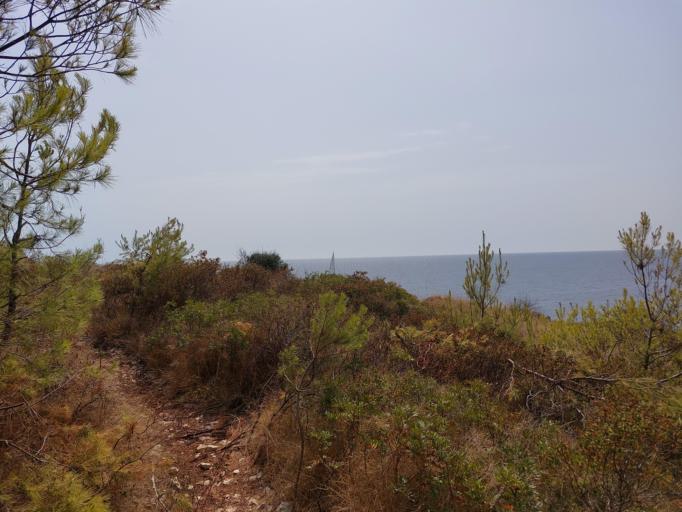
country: HR
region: Dubrovacko-Neretvanska
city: Smokvica
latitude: 42.7256
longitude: 16.8817
